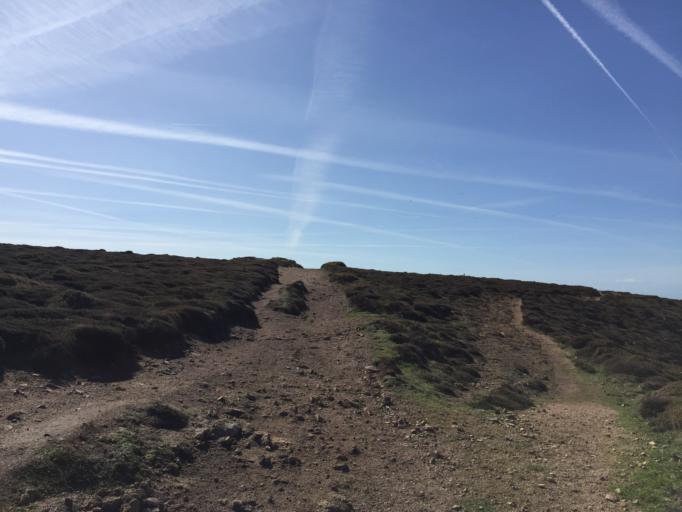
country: JE
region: St Helier
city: Saint Helier
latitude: 49.2499
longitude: -2.2513
